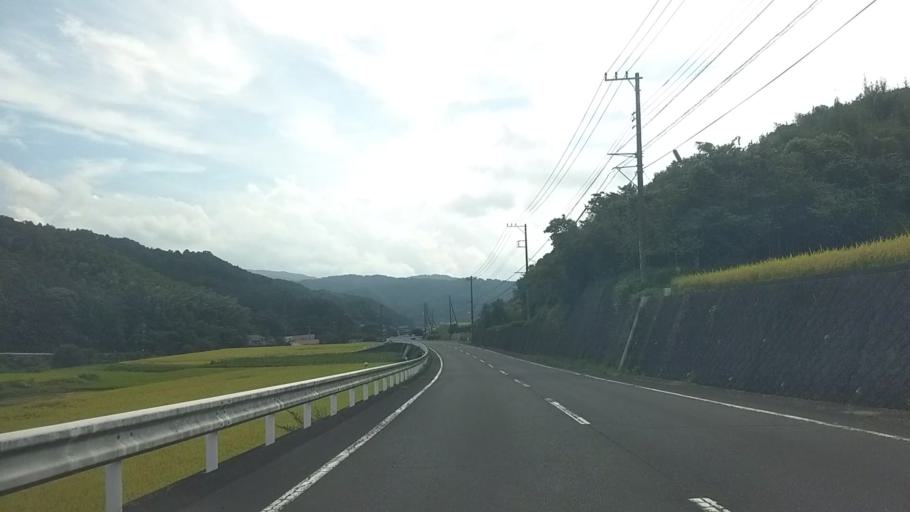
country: JP
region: Shizuoka
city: Ito
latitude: 34.9838
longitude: 138.9819
